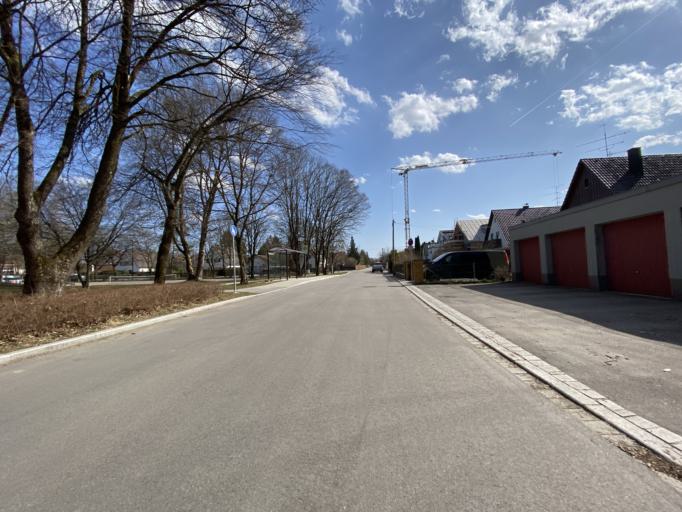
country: DE
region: Bavaria
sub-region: Upper Bavaria
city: Aschheim
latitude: 48.1525
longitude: 11.6931
